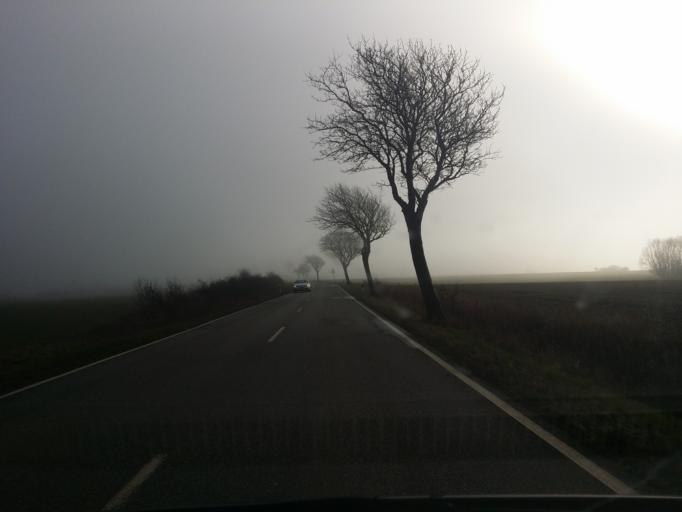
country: DE
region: Schleswig-Holstein
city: Fehmarn
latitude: 54.4395
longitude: 11.1377
